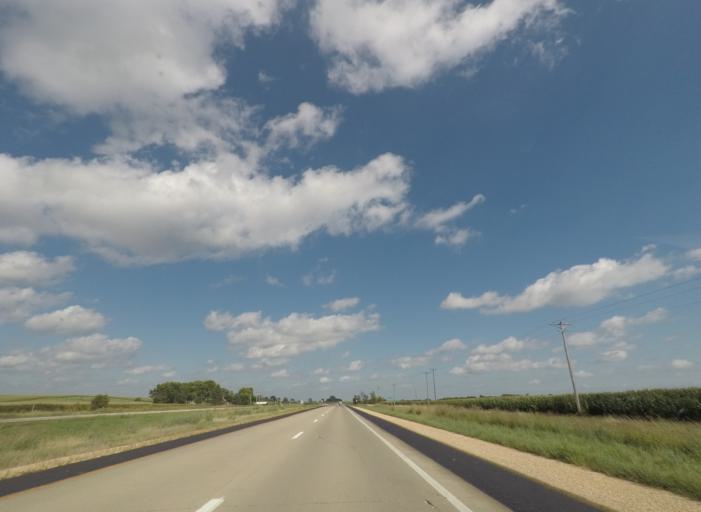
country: US
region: Iowa
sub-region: Dubuque County
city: Cascade
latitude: 42.2855
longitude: -91.0890
